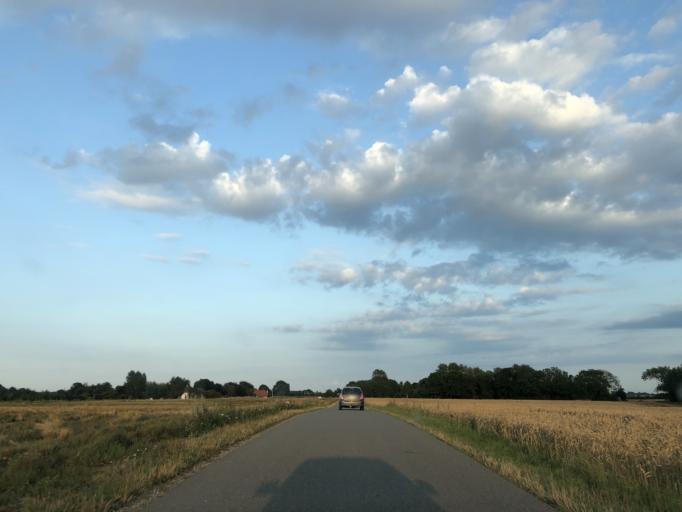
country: DK
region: South Denmark
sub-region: Kerteminde Kommune
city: Munkebo
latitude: 55.5132
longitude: 10.5989
